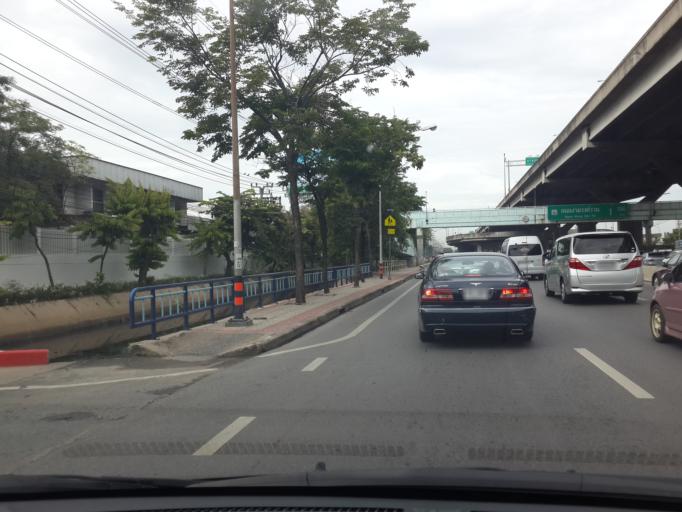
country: TH
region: Bangkok
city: Lak Si
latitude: 13.8622
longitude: 100.5696
